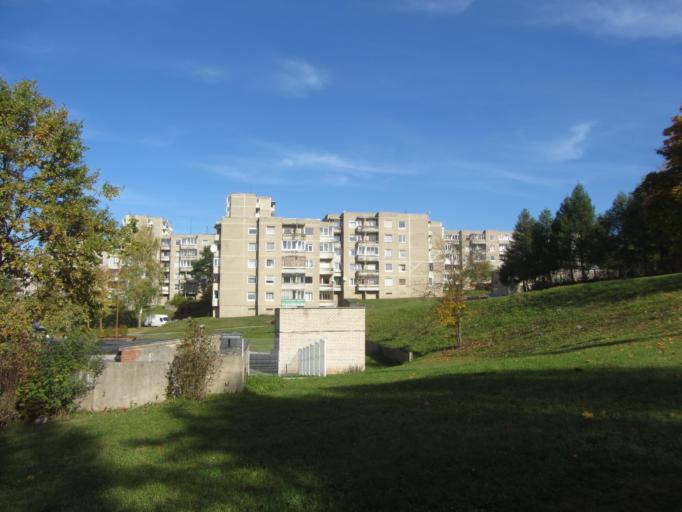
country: LT
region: Vilnius County
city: Elektrenai
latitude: 54.7857
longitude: 24.6759
